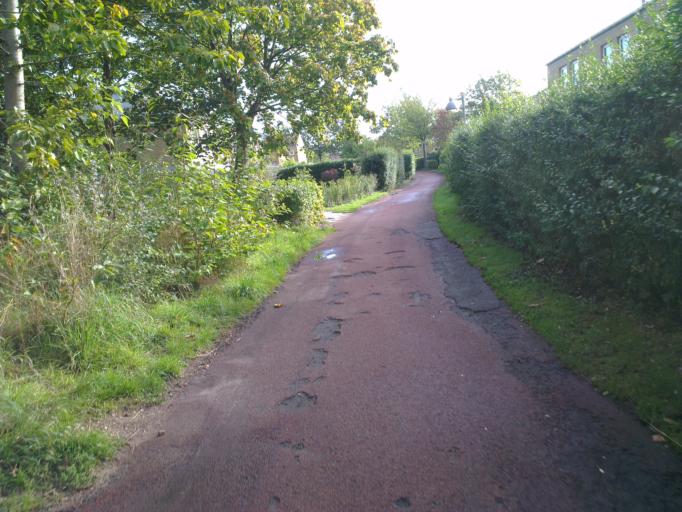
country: DK
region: Capital Region
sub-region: Frederikssund Kommune
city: Frederikssund
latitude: 55.8584
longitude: 12.0744
